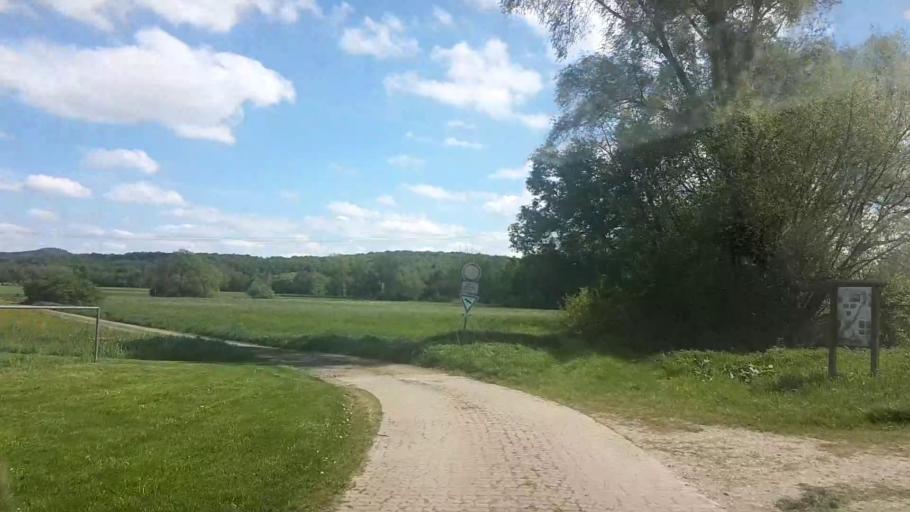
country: DE
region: Bavaria
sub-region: Regierungsbezirk Unterfranken
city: Untermerzbach
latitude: 50.1520
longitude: 10.9050
